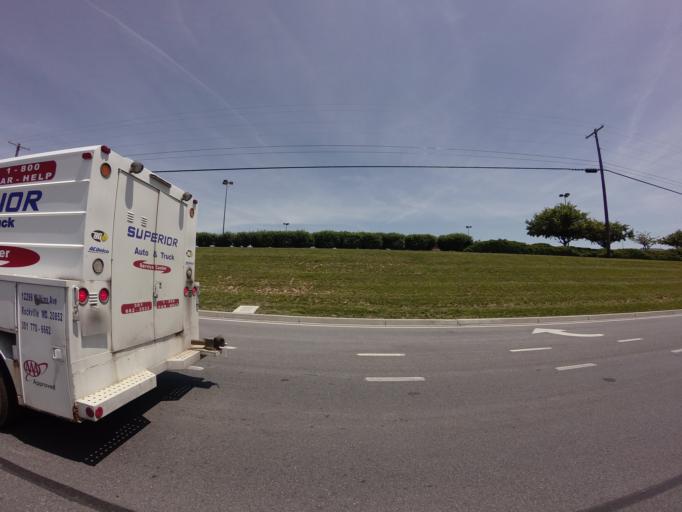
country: US
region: Maryland
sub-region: Frederick County
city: Frederick
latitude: 39.3849
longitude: -77.4022
